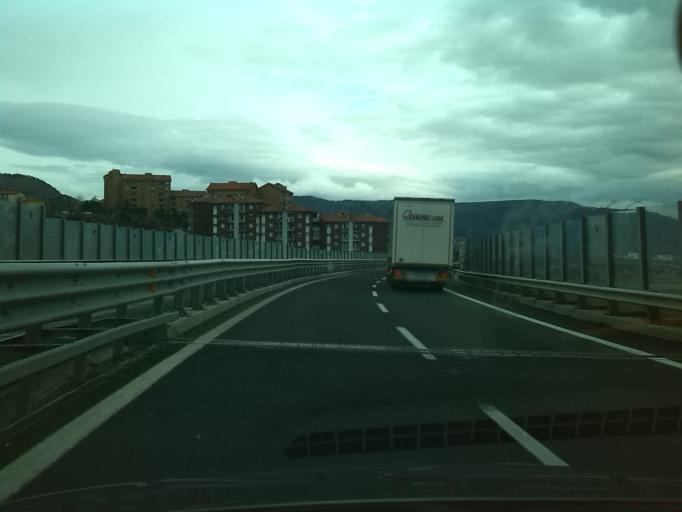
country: IT
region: Friuli Venezia Giulia
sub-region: Provincia di Trieste
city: Domio
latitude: 45.6322
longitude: 13.8169
